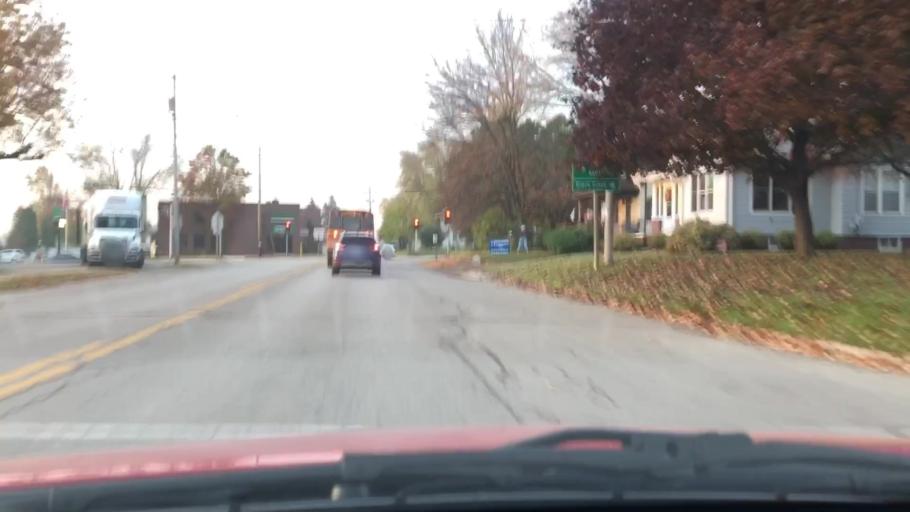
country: US
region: Wisconsin
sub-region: Outagamie County
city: Seymour
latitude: 44.5014
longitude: -88.3308
